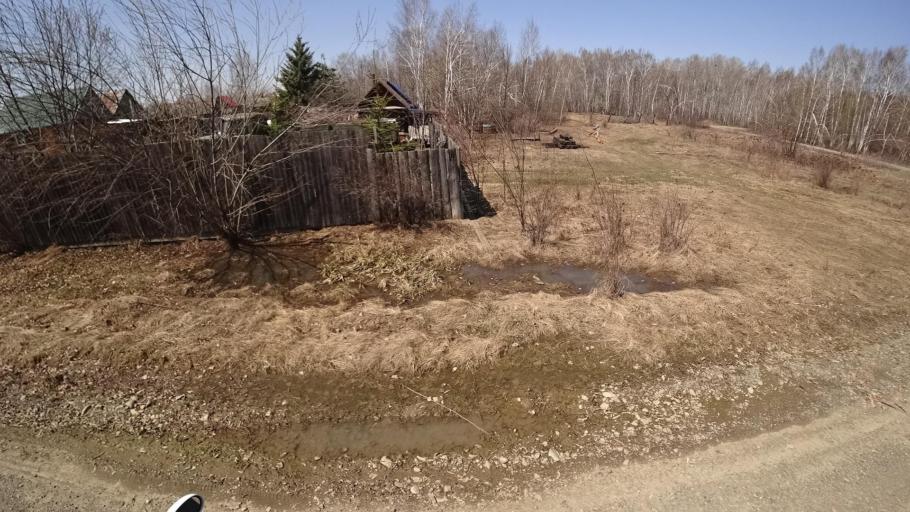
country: RU
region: Khabarovsk Krai
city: Khurba
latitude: 50.4152
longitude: 136.8623
